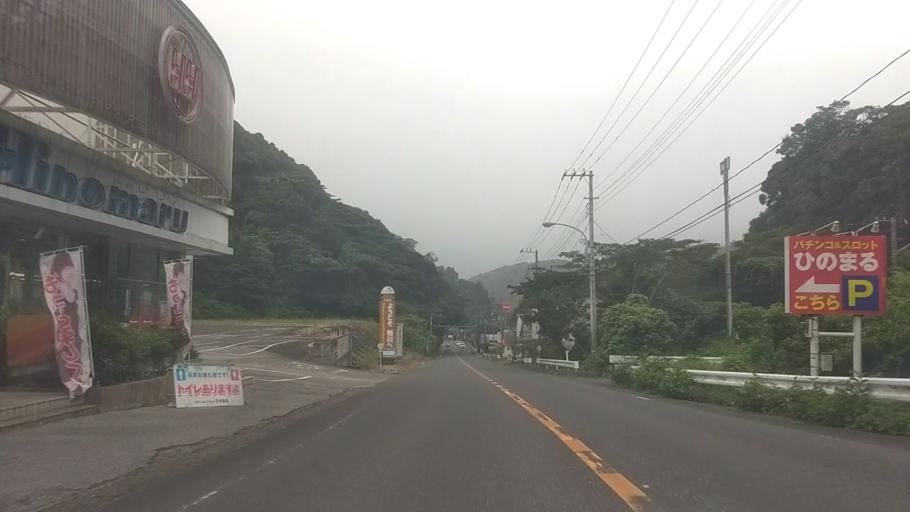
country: JP
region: Chiba
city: Kawaguchi
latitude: 35.1189
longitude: 140.2053
